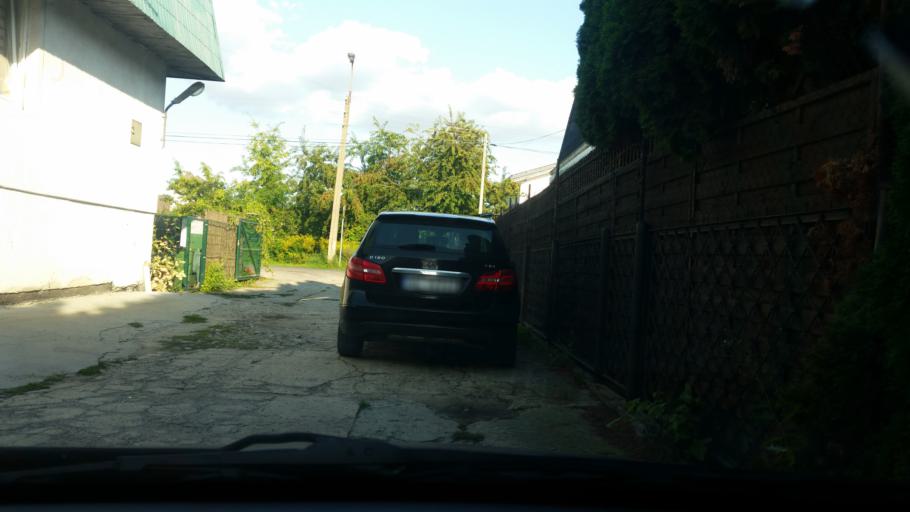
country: PL
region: Masovian Voivodeship
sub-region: Warszawa
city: Bemowo
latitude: 52.2451
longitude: 20.8858
